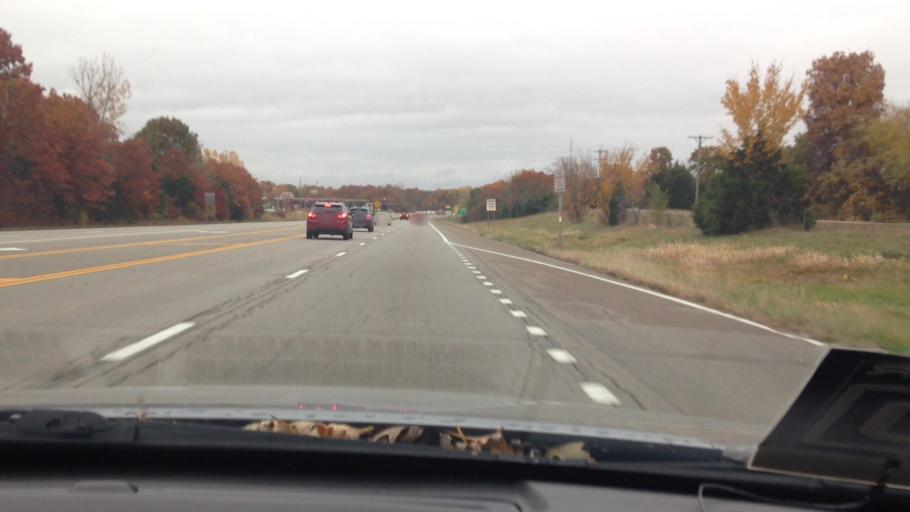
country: US
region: Kansas
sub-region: Wyandotte County
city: Bonner Springs
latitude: 39.1085
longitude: -94.8868
